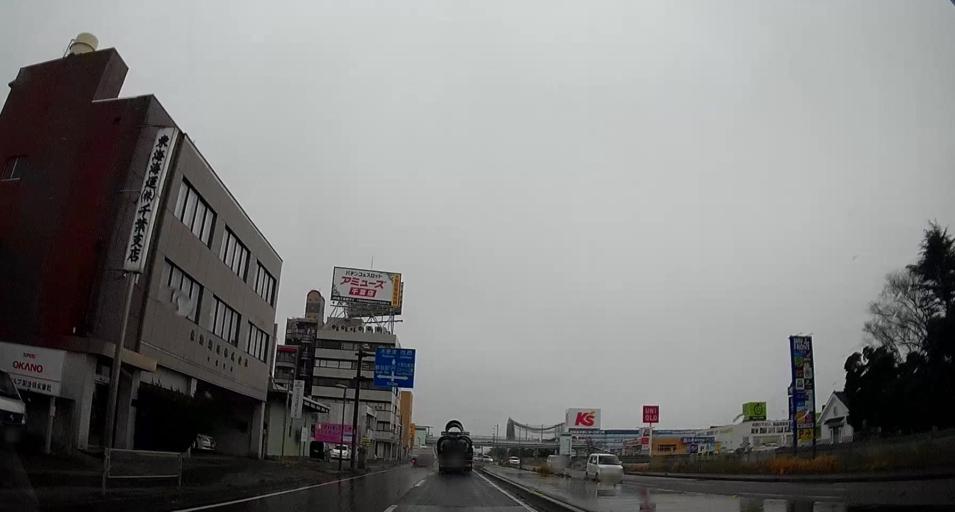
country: JP
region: Chiba
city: Chiba
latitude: 35.5819
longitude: 140.1261
